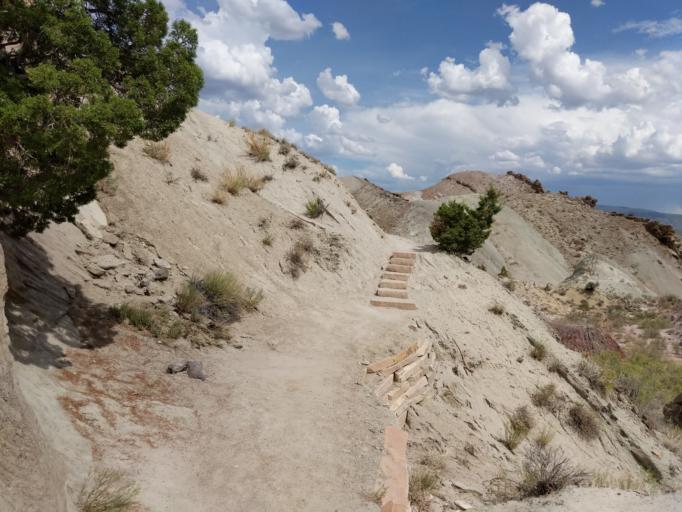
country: US
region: Utah
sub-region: Uintah County
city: Naples
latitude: 40.4412
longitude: -109.3007
